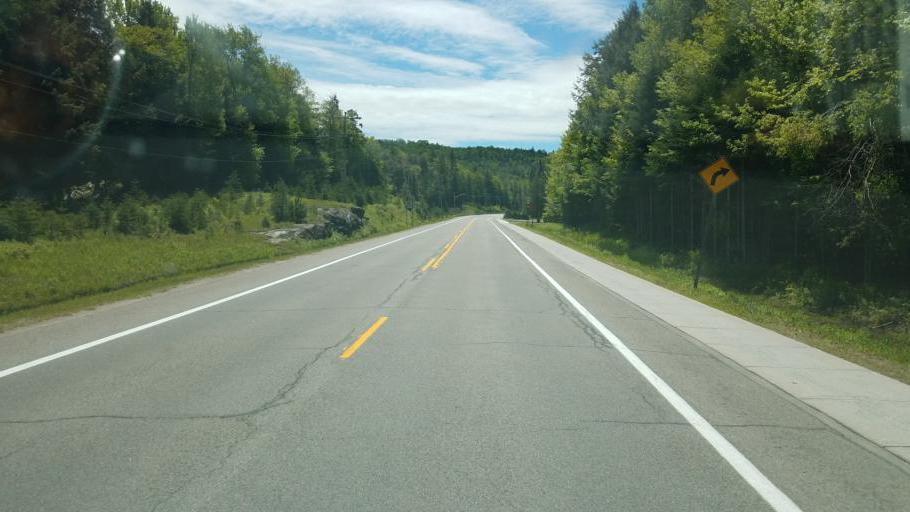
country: US
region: New York
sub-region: Hamilton County
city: Lake Pleasant
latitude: 43.7609
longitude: -74.7923
